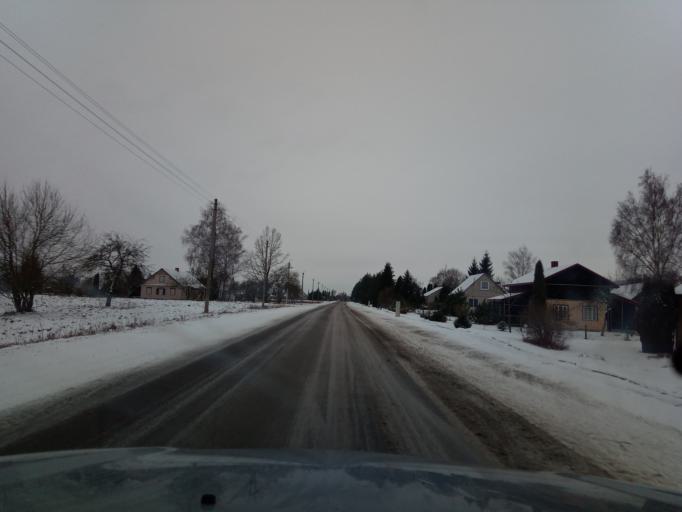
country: LT
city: Ramygala
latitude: 55.4933
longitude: 24.4894
